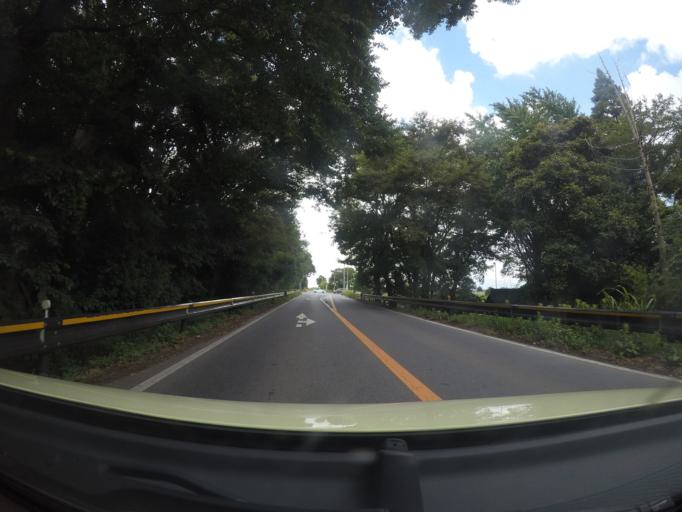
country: JP
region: Ibaraki
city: Mitsukaido
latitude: 36.0635
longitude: 139.9800
